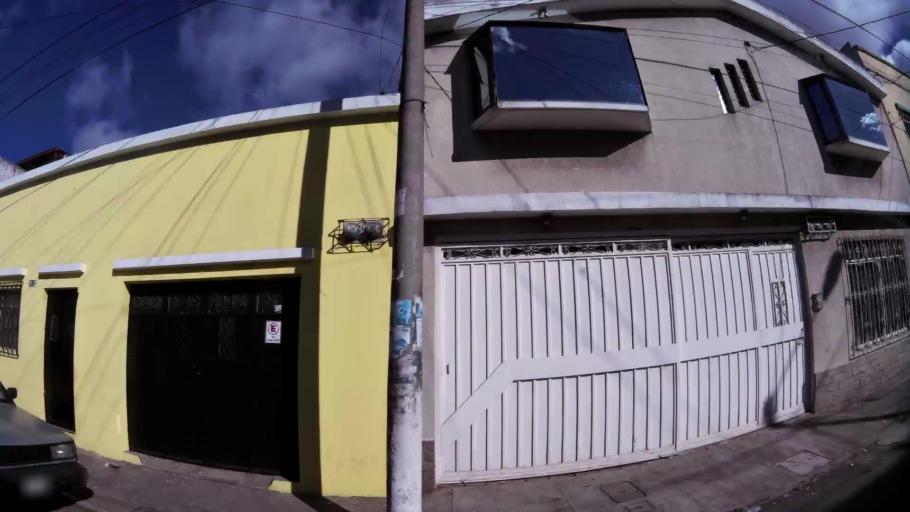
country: GT
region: Guatemala
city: Guatemala City
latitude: 14.6194
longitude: -90.5014
